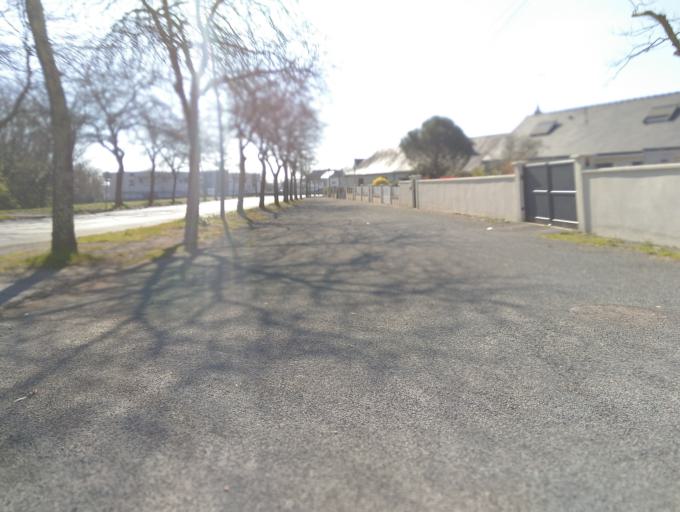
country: FR
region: Pays de la Loire
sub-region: Departement de Maine-et-Loire
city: Les Ponts-de-Ce
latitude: 47.4554
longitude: -0.5073
